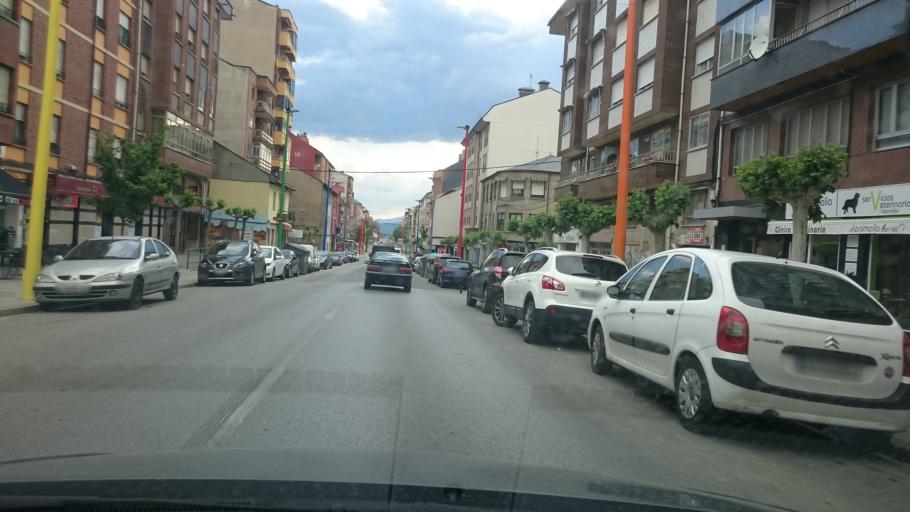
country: ES
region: Castille and Leon
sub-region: Provincia de Leon
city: Ponferrada
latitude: 42.5455
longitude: -6.6128
